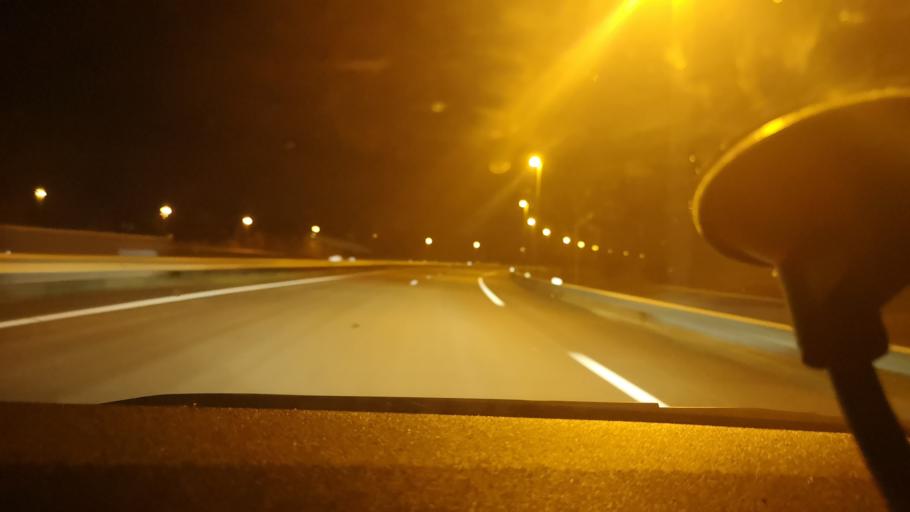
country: FR
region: Bourgogne
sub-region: Departement de la Cote-d'Or
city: Beaune
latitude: 47.0593
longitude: 4.9109
